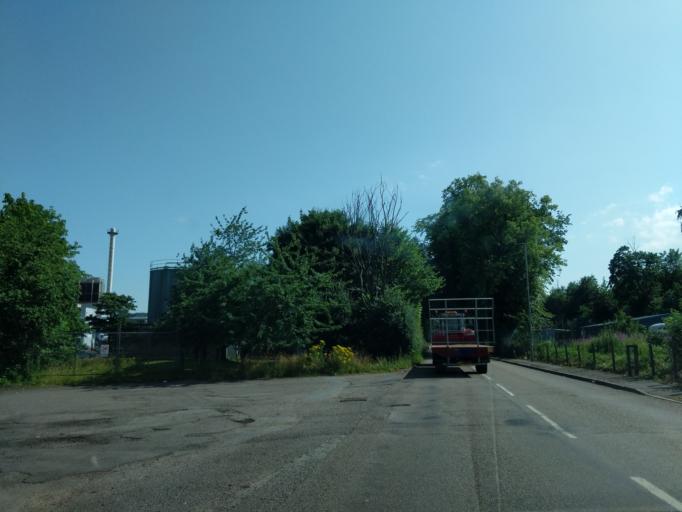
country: GB
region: Scotland
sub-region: Moray
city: Rothes
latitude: 57.5342
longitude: -3.2080
